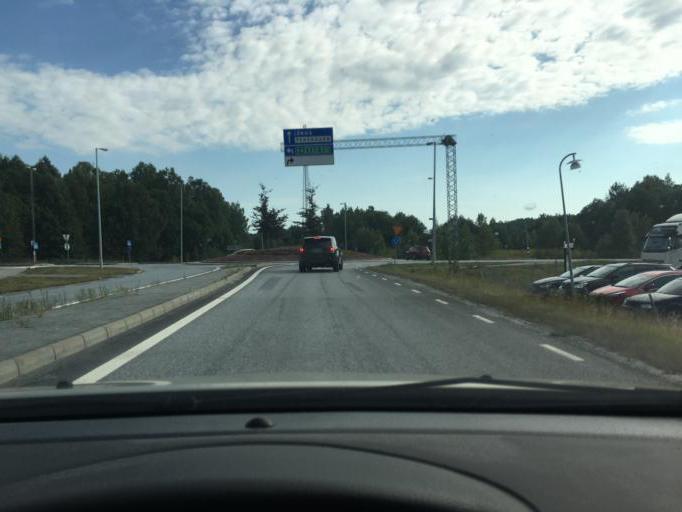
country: SE
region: Stockholm
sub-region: Sodertalje Kommun
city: Pershagen
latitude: 59.1587
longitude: 17.6424
